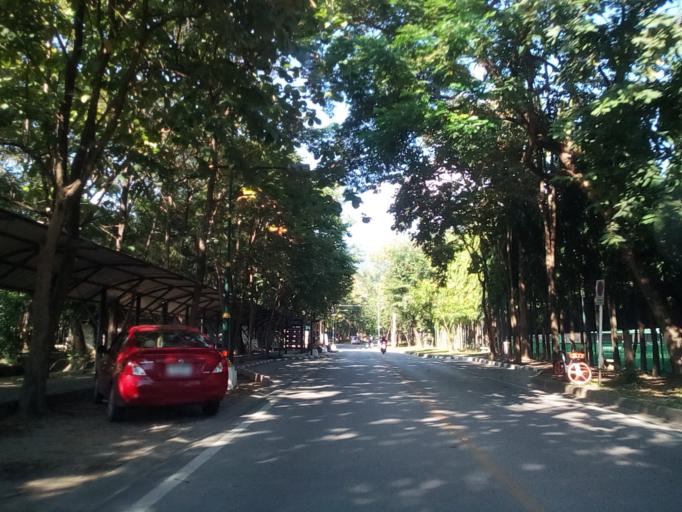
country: TH
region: Chiang Mai
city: Chiang Mai
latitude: 18.7995
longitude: 98.9567
